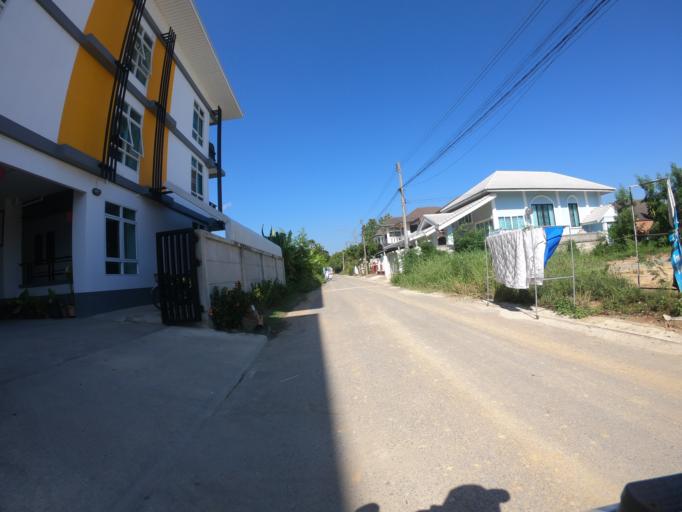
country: TH
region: Chiang Mai
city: Chiang Mai
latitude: 18.7418
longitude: 98.9648
